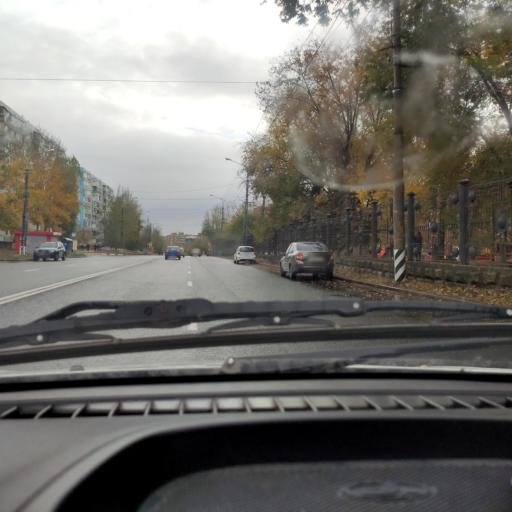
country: RU
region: Samara
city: Zhigulevsk
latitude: 53.4822
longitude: 49.4661
